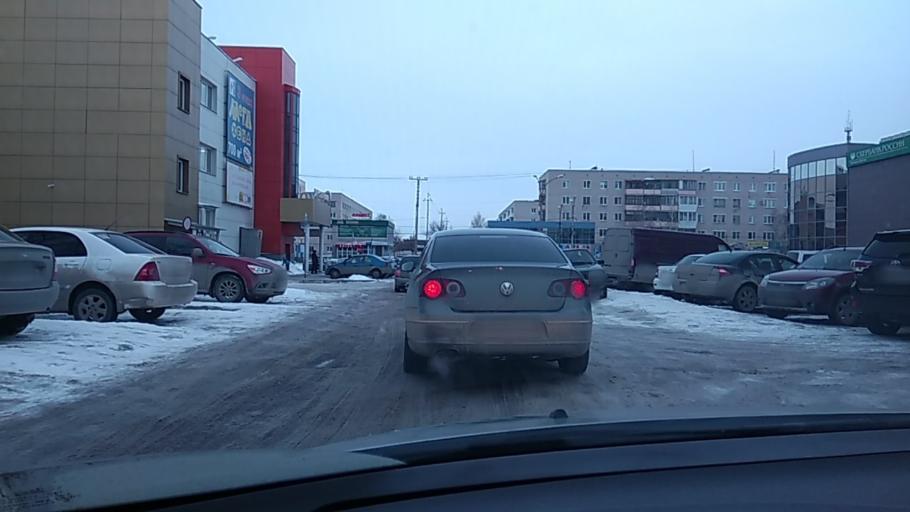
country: RU
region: Sverdlovsk
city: Kamensk-Ural'skiy
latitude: 56.4236
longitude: 61.9067
